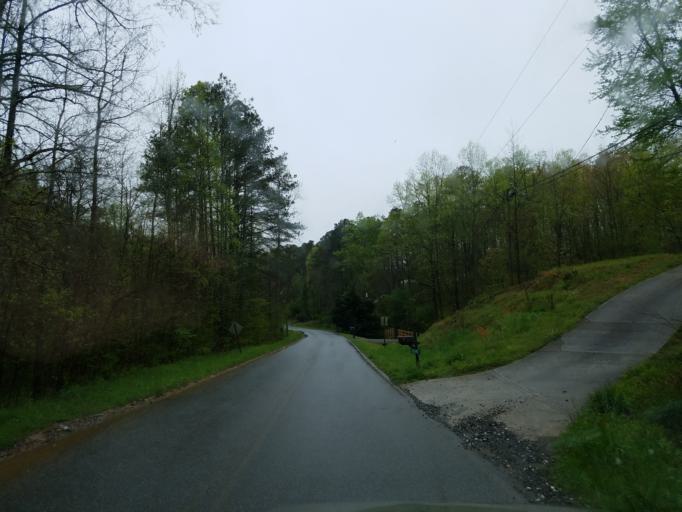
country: US
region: Georgia
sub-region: Gilmer County
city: Ellijay
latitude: 34.5667
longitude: -84.5248
